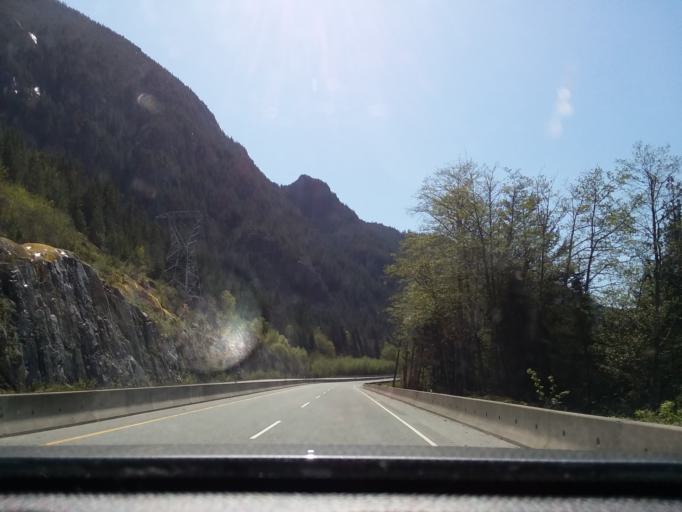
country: CA
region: British Columbia
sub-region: Greater Vancouver Regional District
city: Lions Bay
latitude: 49.6673
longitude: -123.1682
